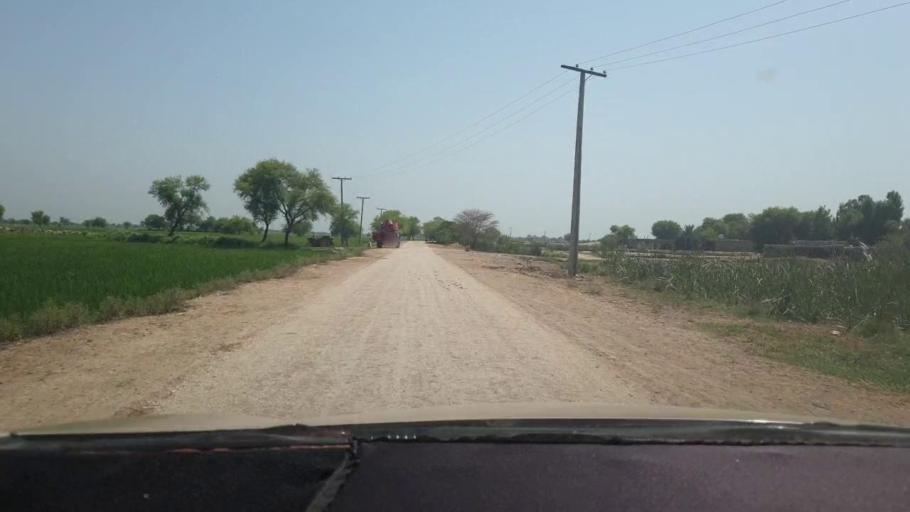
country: PK
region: Sindh
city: Miro Khan
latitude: 27.6822
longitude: 68.0953
